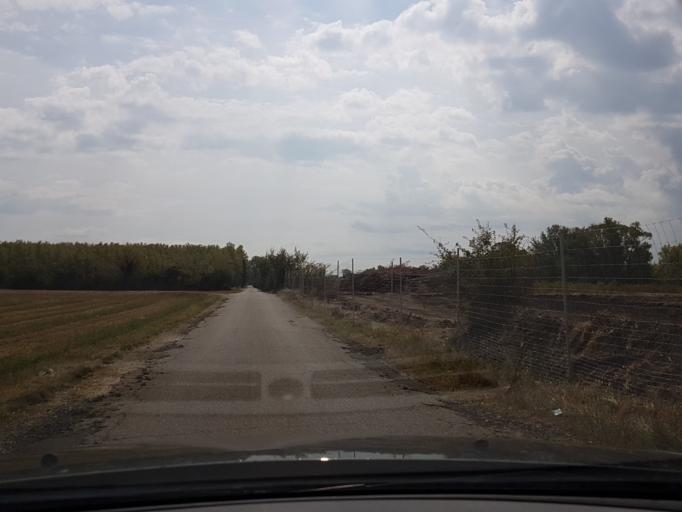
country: FR
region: Provence-Alpes-Cote d'Azur
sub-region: Departement du Vaucluse
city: Saint-Saturnin-les-Avignon
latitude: 43.9796
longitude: 4.9387
